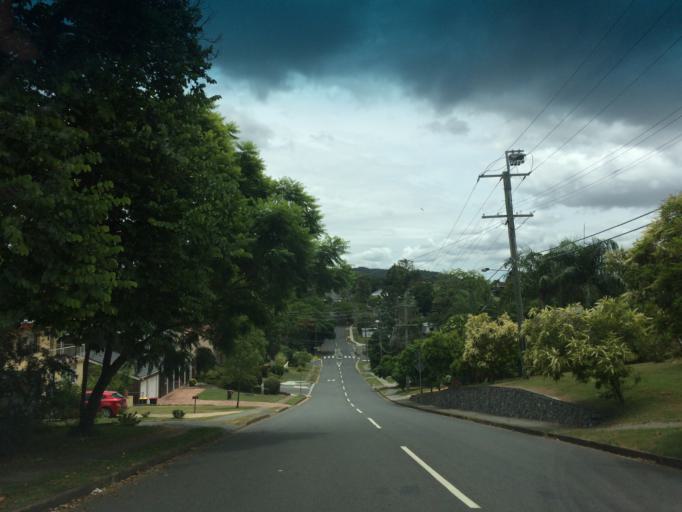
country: AU
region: Queensland
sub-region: Brisbane
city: Kenmore Hills
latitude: -27.5191
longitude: 152.9459
